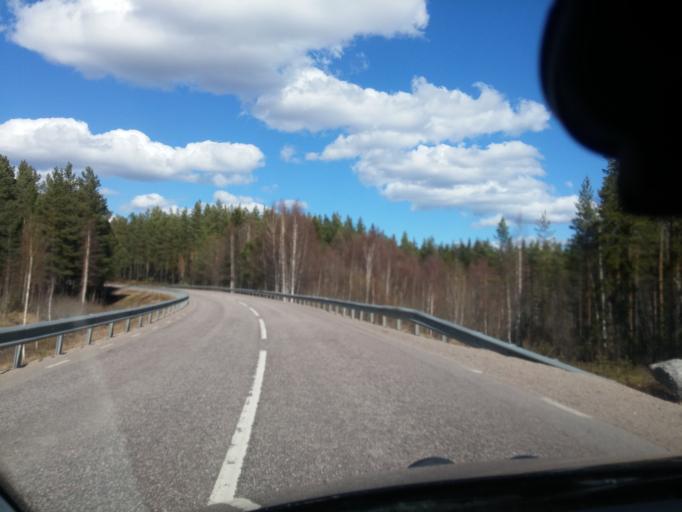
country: SE
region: Gaevleborg
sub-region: Ovanakers Kommun
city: Edsbyn
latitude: 61.2494
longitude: 15.8926
